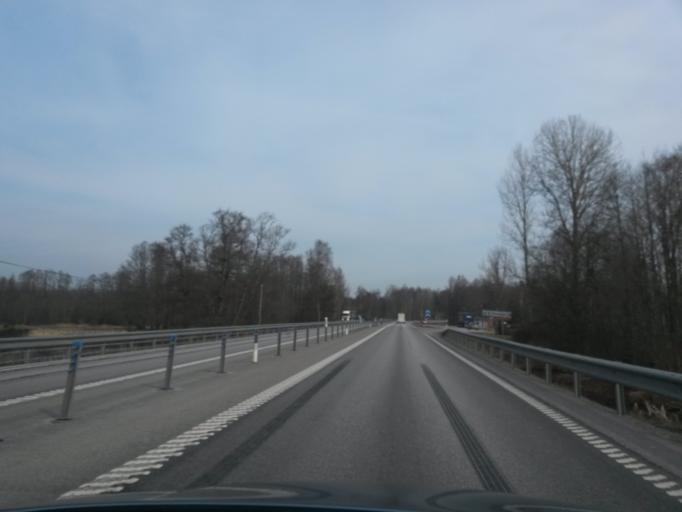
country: SE
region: OErebro
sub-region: Laxa Kommun
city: Laxa
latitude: 58.9685
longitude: 14.5384
